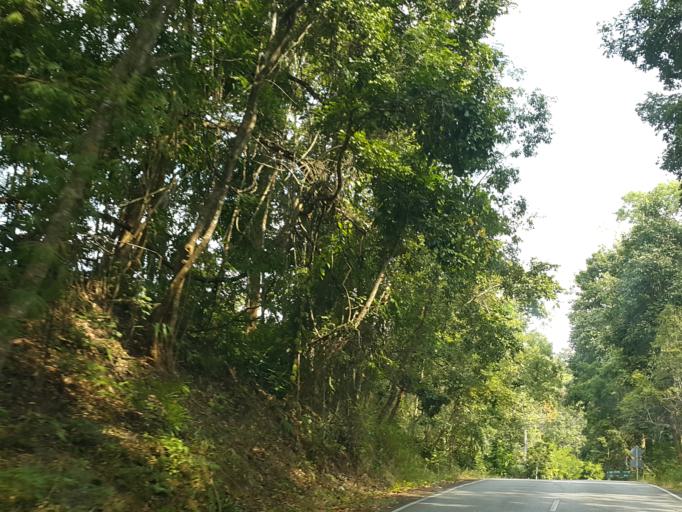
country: TH
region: Chiang Mai
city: Mae On
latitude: 18.8637
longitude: 99.2872
